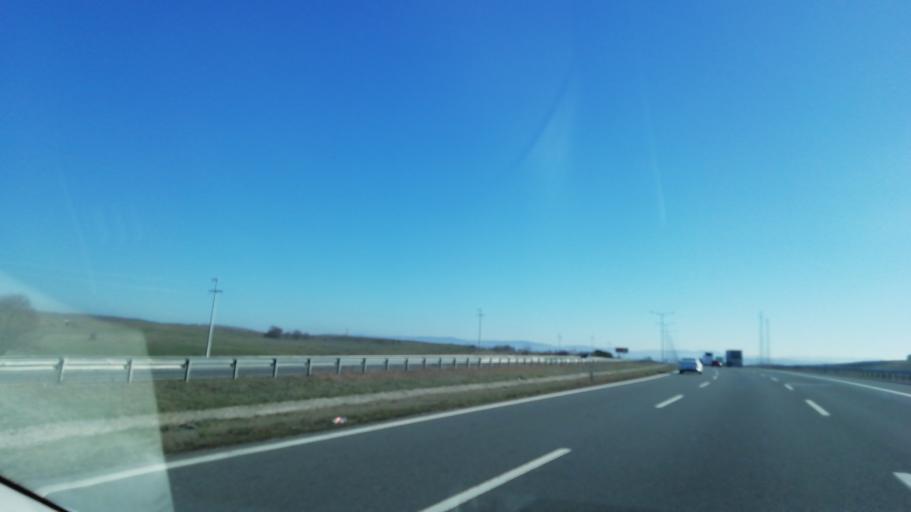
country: TR
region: Bolu
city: Yenicaga
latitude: 40.7565
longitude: 32.0664
